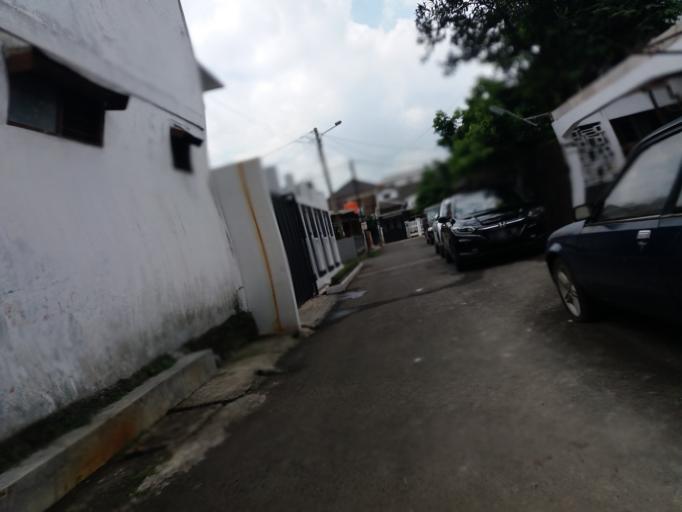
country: ID
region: West Java
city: Bandung
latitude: -6.9210
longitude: 107.6566
